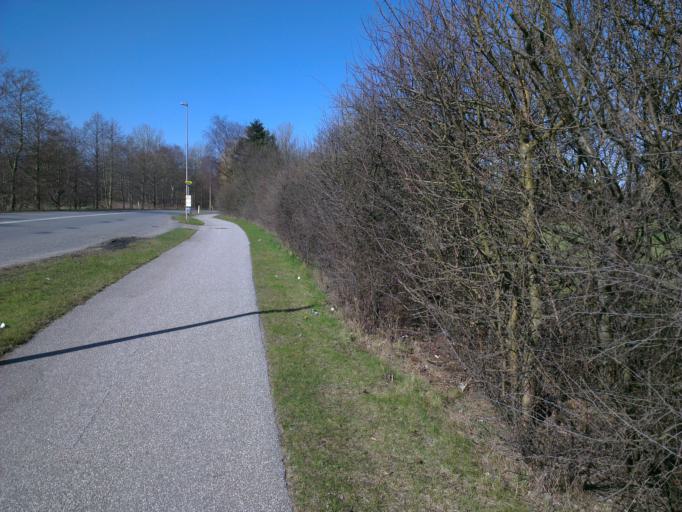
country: DK
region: Capital Region
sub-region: Frederikssund Kommune
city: Frederikssund
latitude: 55.8550
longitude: 12.0730
